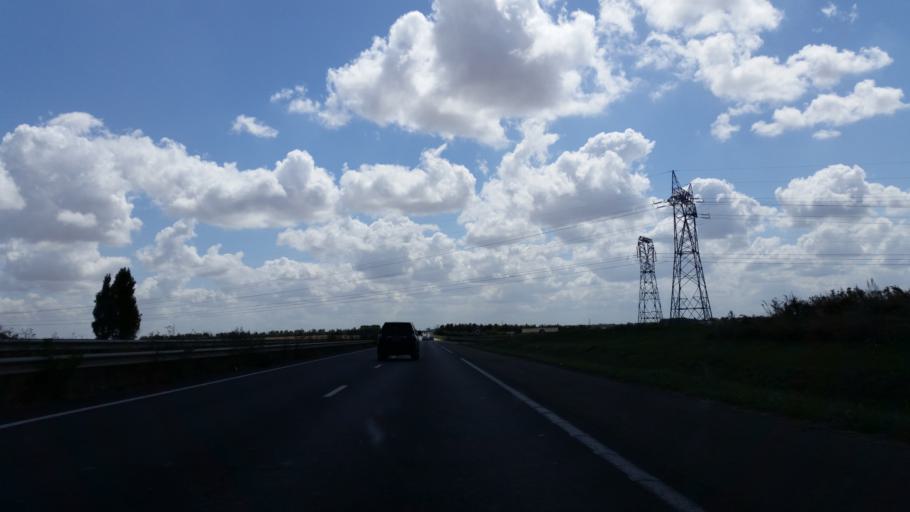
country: FR
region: Lower Normandy
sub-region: Departement du Calvados
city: Ifs
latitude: 49.1355
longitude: -0.3333
